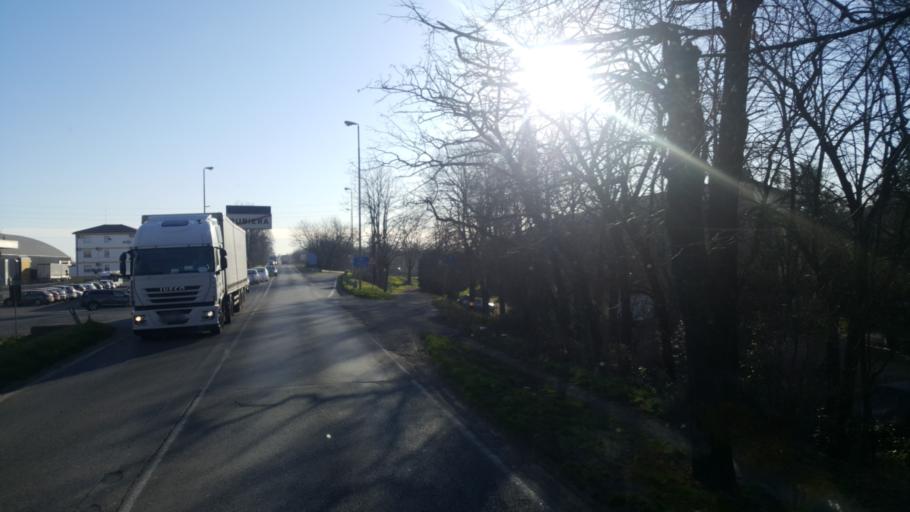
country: IT
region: Emilia-Romagna
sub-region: Provincia di Reggio Emilia
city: Rubiera
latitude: 44.6518
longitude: 10.7890
